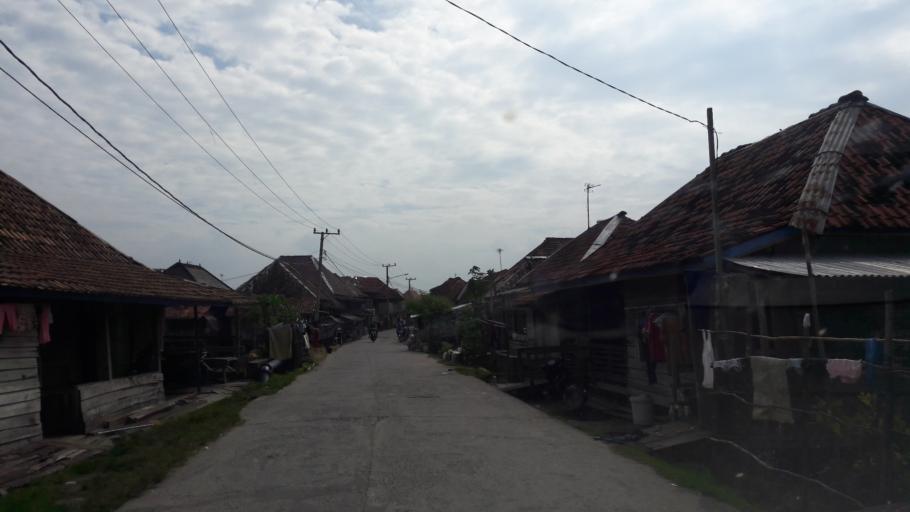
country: ID
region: South Sumatra
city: Gunungmenang
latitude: -3.0903
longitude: 104.0250
